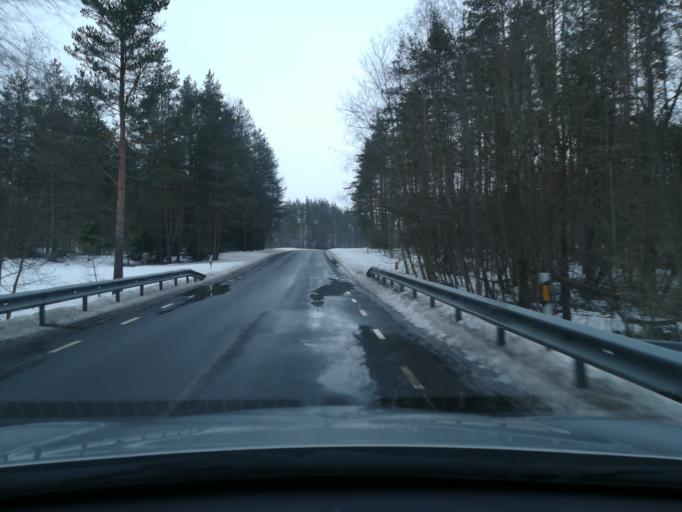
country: EE
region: Harju
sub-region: Kuusalu vald
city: Kuusalu
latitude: 59.4633
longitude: 25.5023
